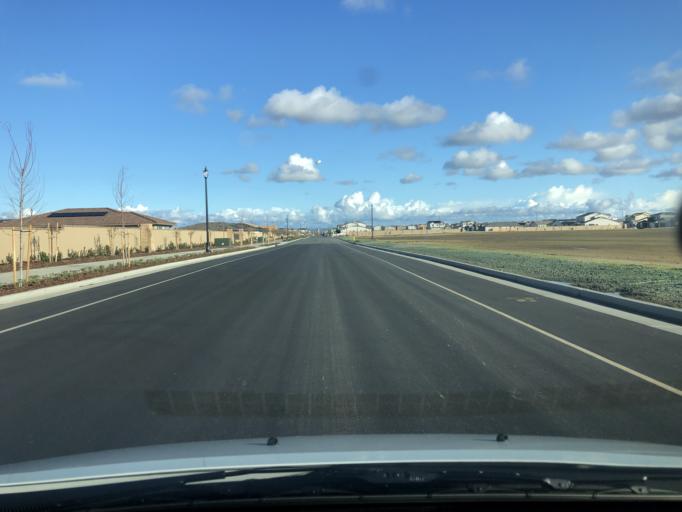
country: US
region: California
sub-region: Sacramento County
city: North Highlands
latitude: 38.7710
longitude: -121.3928
